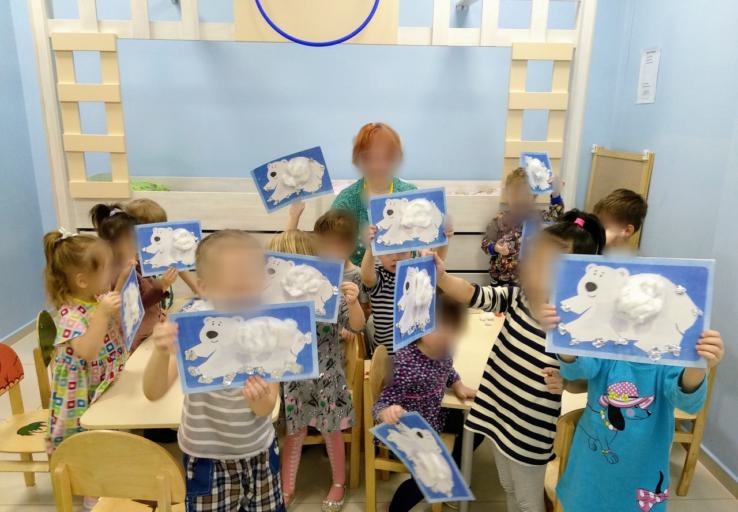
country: RU
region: Moskovskaya
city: Reutov
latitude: 55.7531
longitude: 37.8695
